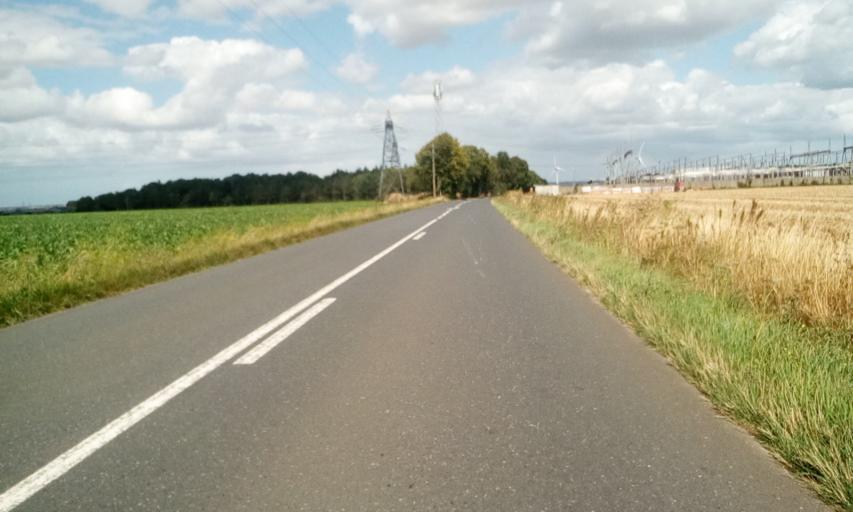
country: FR
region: Lower Normandy
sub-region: Departement du Calvados
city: Bourguebus
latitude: 49.1052
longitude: -0.2680
